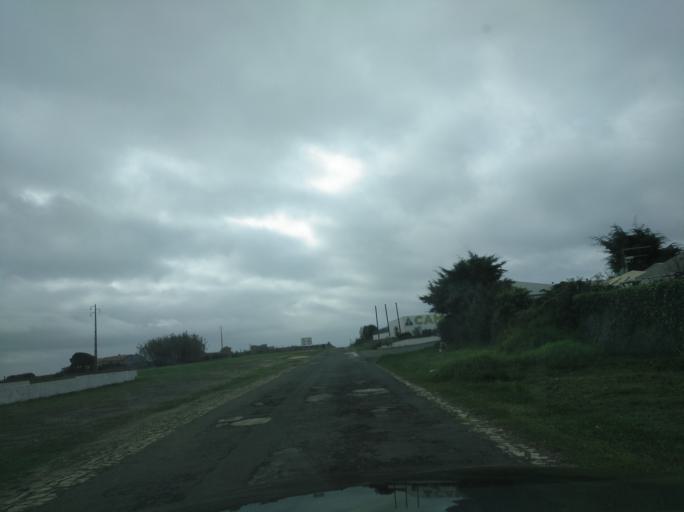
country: PT
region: Setubal
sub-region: Sines
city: Porto Covo
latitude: 37.8420
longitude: -8.7797
